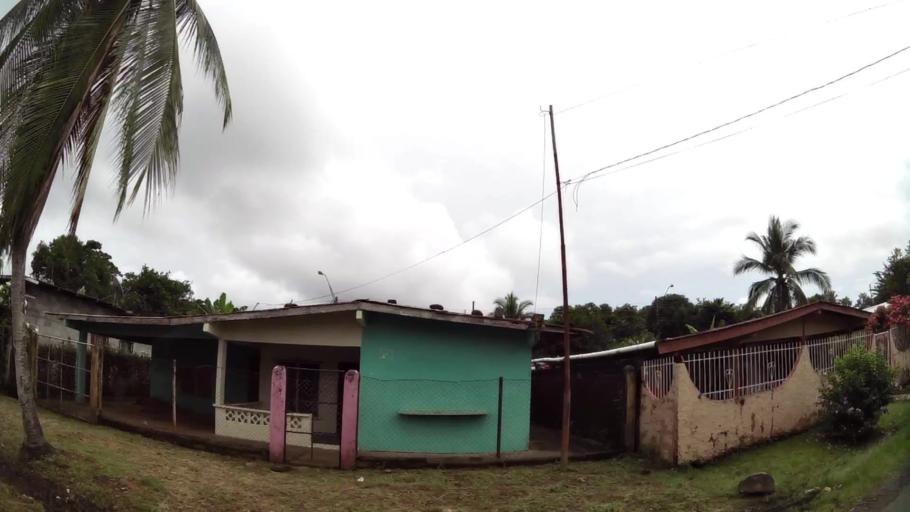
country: PA
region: Chiriqui
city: David
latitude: 8.4172
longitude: -82.4467
